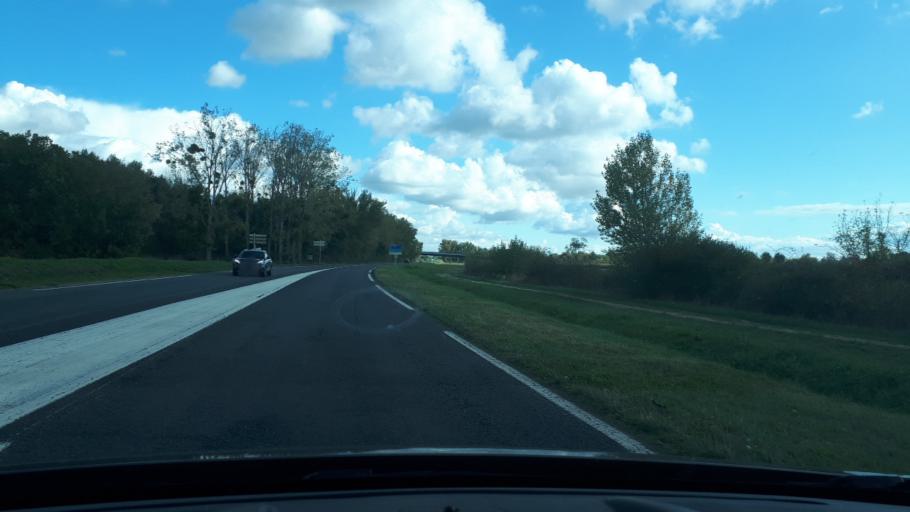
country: FR
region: Centre
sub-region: Departement du Loir-et-Cher
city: Mareuil-sur-Cher
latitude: 47.3083
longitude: 1.3401
